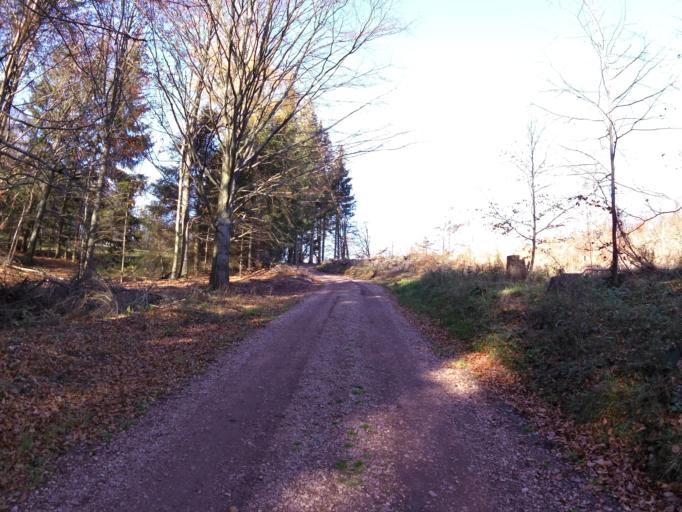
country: DE
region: Thuringia
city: Ruhla
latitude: 50.9042
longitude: 10.3446
